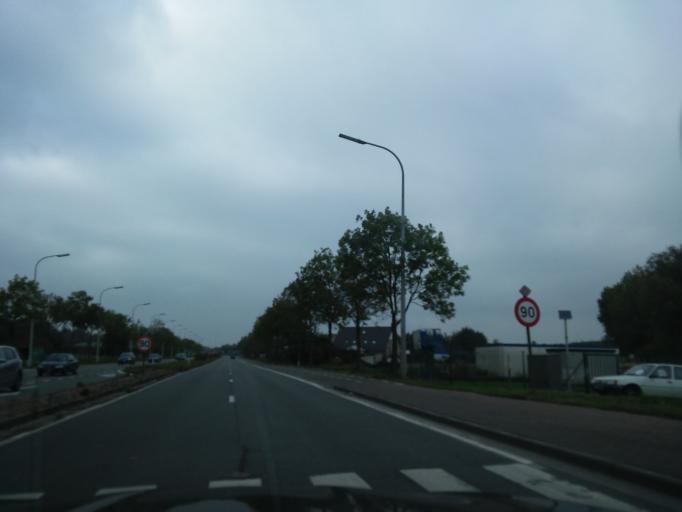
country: BE
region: Flanders
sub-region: Provincie Oost-Vlaanderen
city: Zele
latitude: 51.0795
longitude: 4.0428
